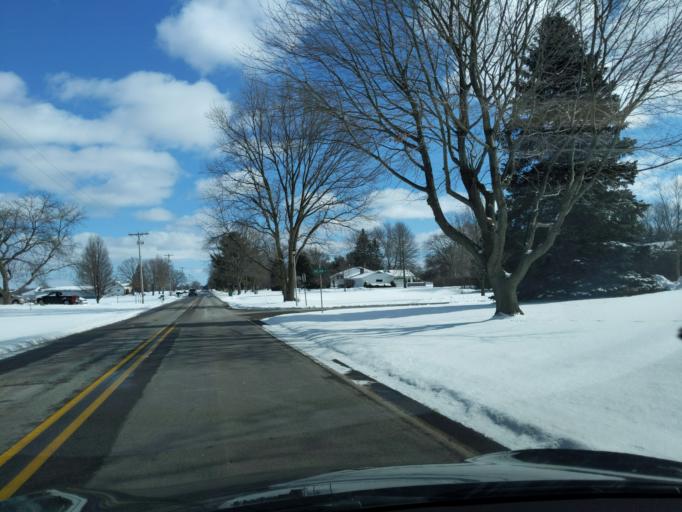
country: US
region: Michigan
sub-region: Eaton County
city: Dimondale
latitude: 42.6474
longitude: -84.6385
